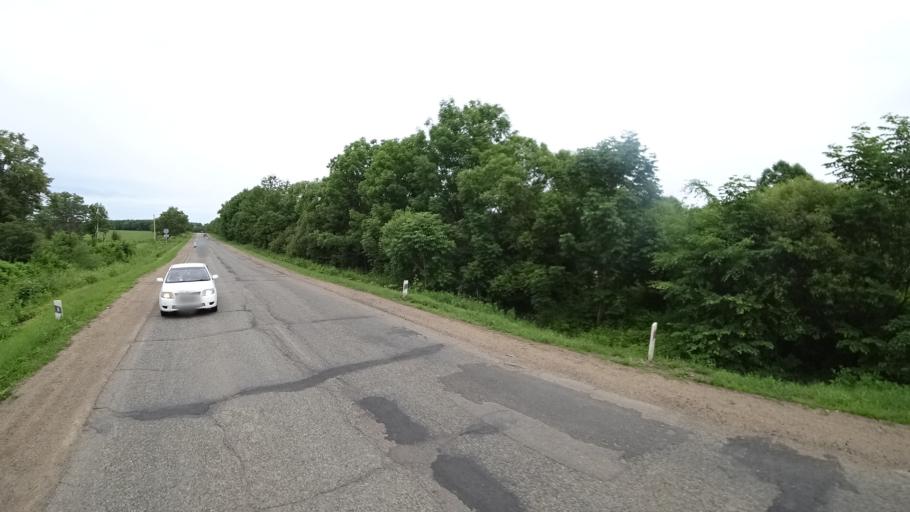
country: RU
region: Primorskiy
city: Novosysoyevka
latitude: 44.1831
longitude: 133.3511
